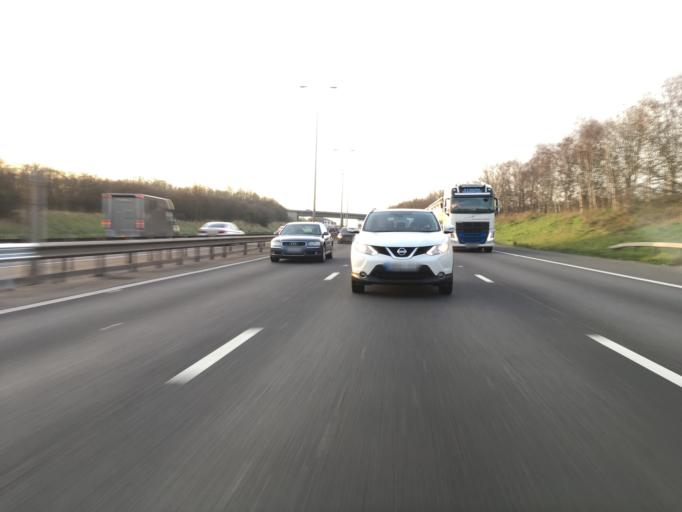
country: GB
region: England
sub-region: Worcestershire
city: Fernhill Heath
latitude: 52.1964
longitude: -2.1672
